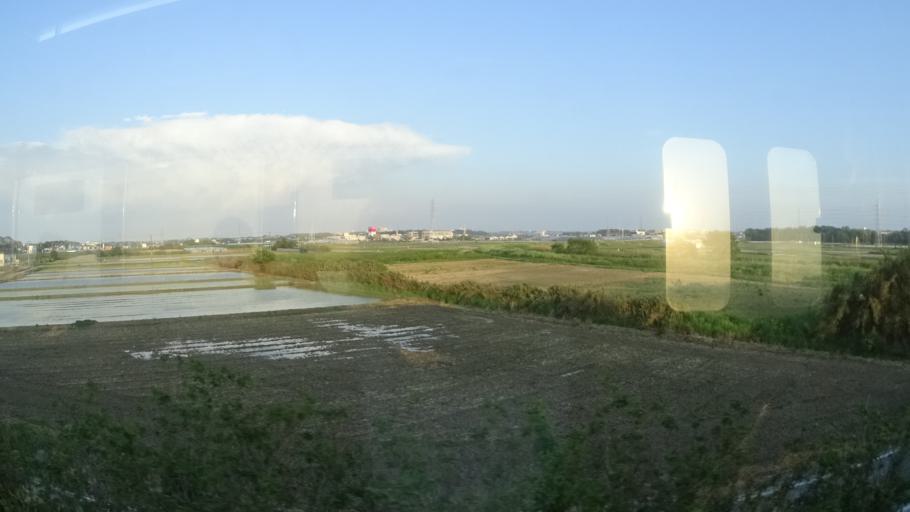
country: JP
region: Aichi
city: Toyohashi
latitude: 34.7142
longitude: 137.3770
